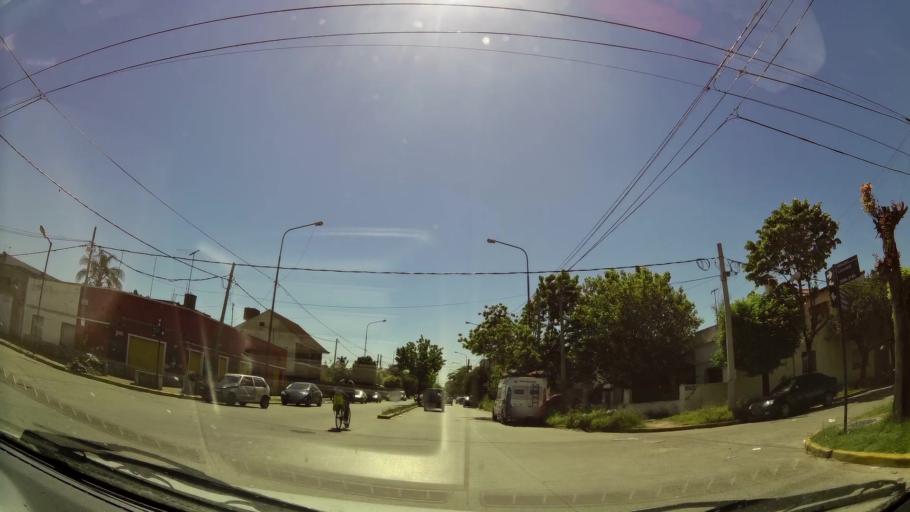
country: AR
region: Buenos Aires
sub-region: Partido de Quilmes
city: Quilmes
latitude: -34.7283
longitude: -58.2986
